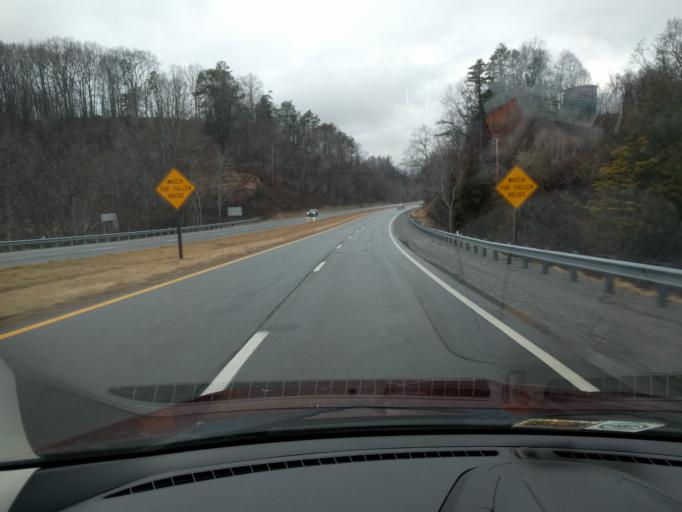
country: US
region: Virginia
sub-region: Montgomery County
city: Prices Fork
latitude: 37.2905
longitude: -80.4995
